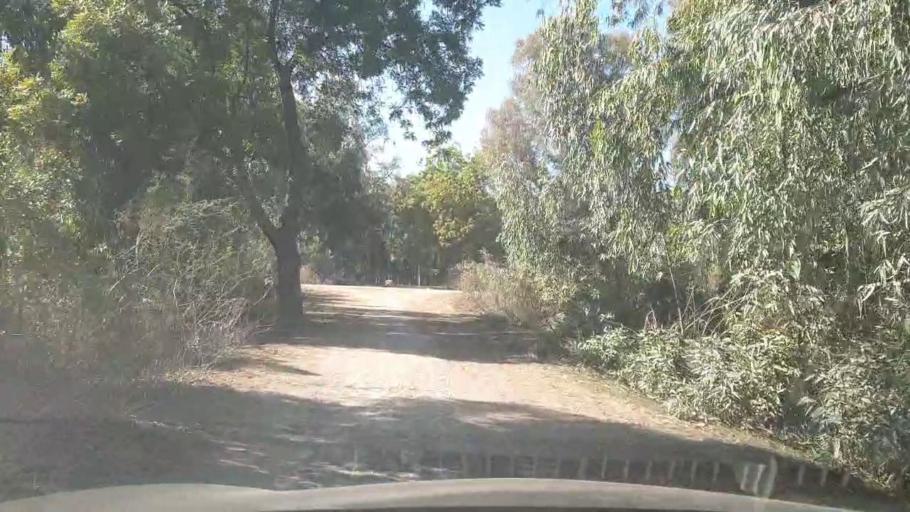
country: PK
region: Sindh
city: Mirpur Mathelo
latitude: 28.0593
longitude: 69.5027
